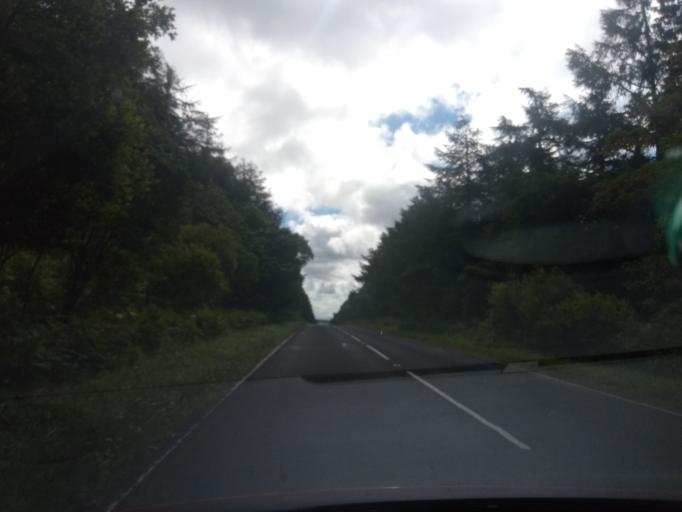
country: GB
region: England
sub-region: Northumberland
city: Rochester
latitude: 55.2960
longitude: -2.3286
